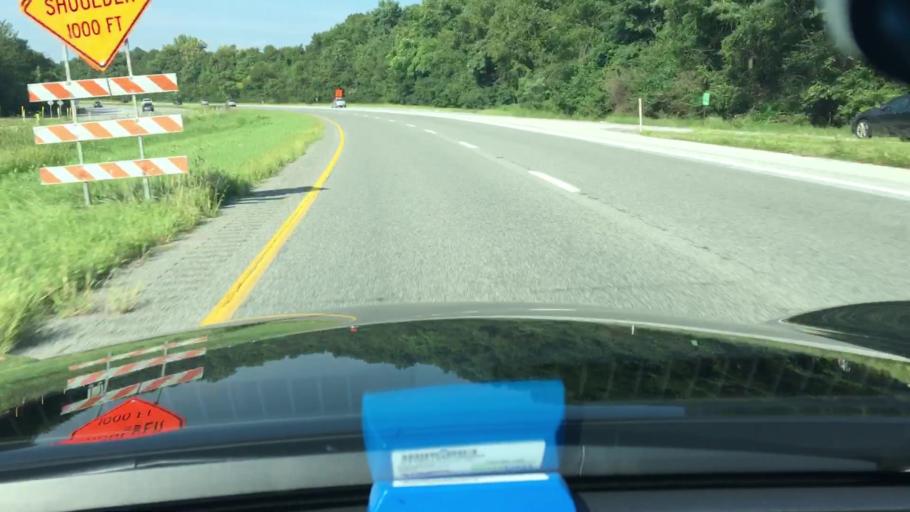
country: US
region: Pennsylvania
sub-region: Chester County
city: Exton
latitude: 40.0068
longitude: -75.5815
